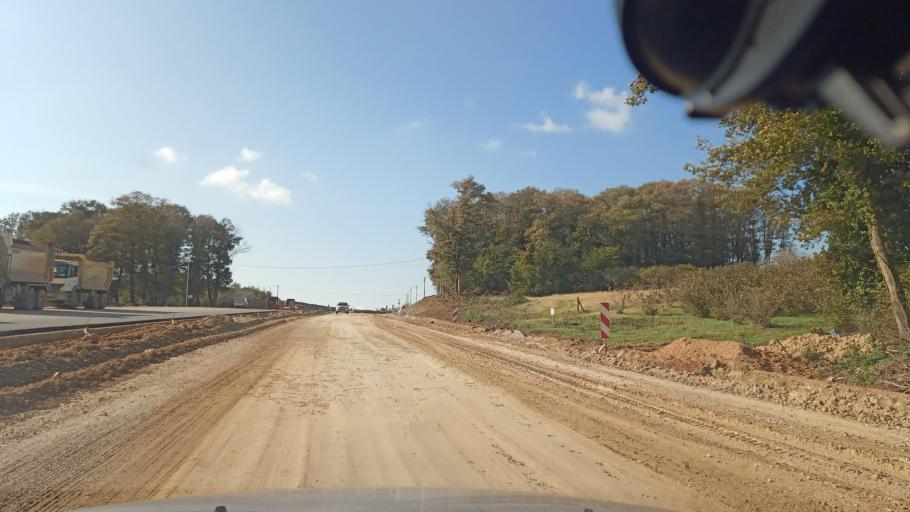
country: TR
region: Sakarya
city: Ferizli
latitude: 41.0999
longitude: 30.4718
